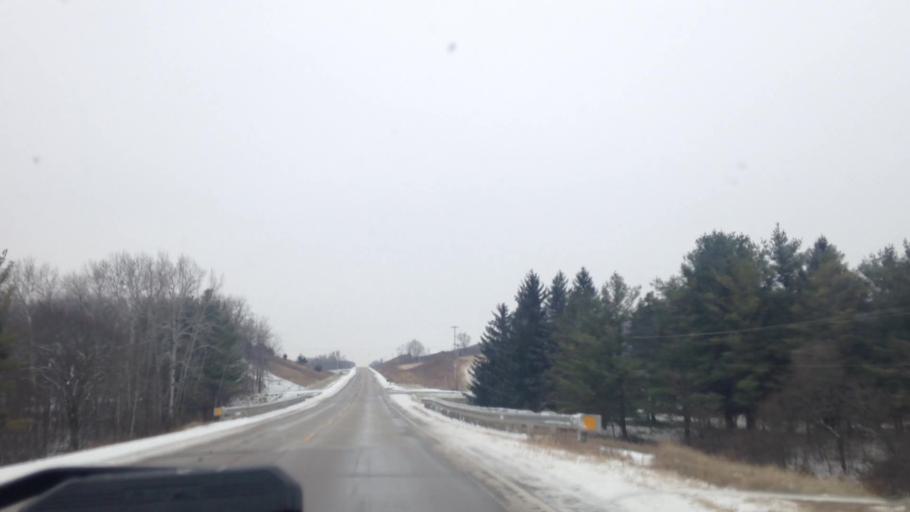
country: US
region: Wisconsin
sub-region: Dodge County
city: Hustisford
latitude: 43.2805
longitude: -88.5185
